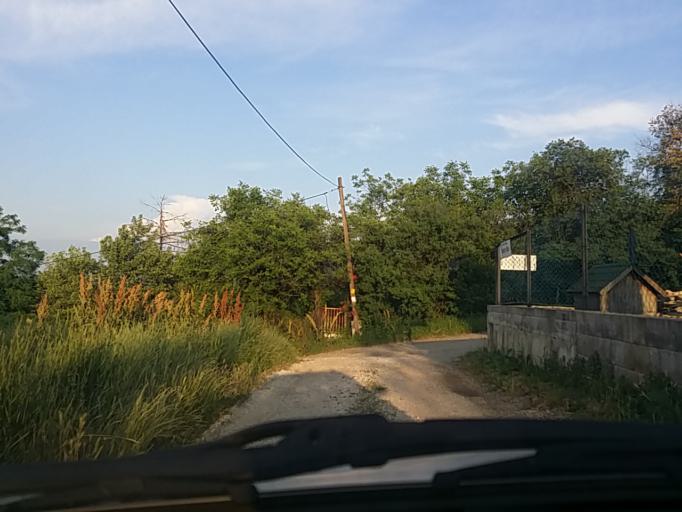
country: HU
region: Pest
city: Urom
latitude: 47.5785
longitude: 19.0256
